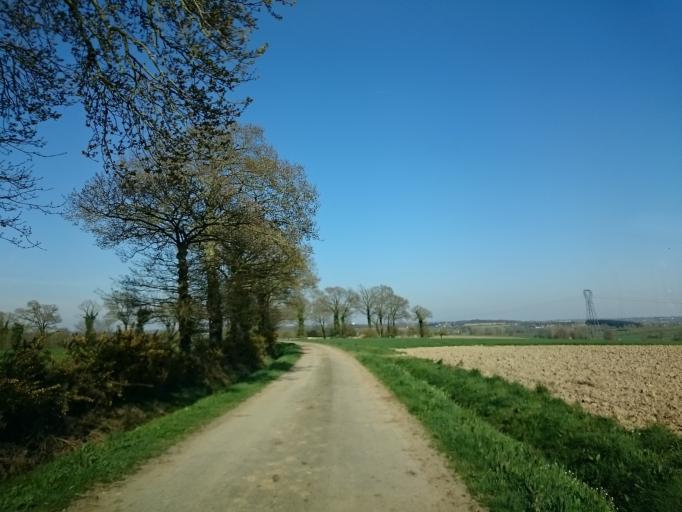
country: FR
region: Brittany
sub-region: Departement d'Ille-et-Vilaine
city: Chanteloup
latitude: 47.9551
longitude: -1.6213
